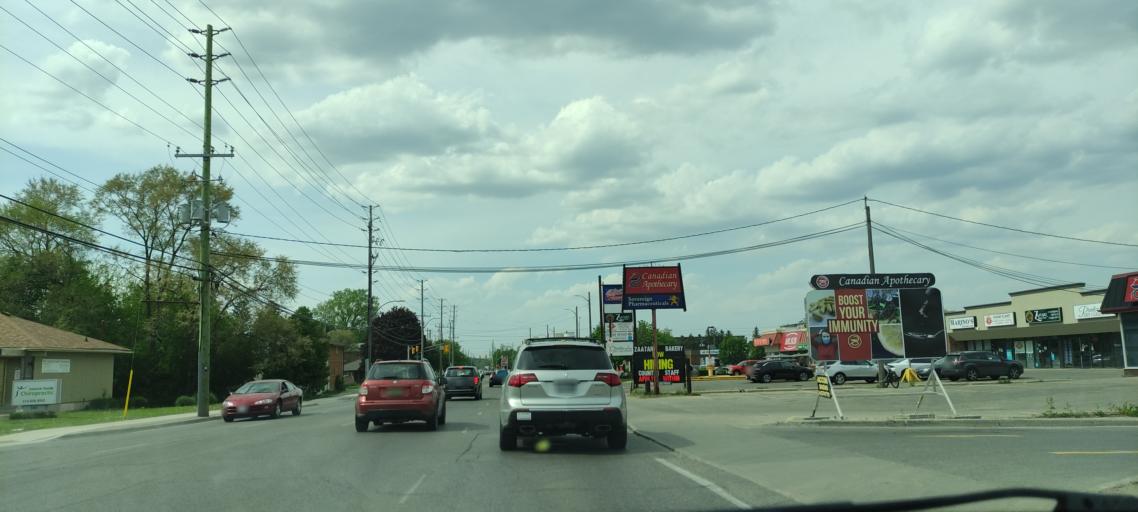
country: CA
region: Ontario
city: London
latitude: 43.0091
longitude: -81.2415
